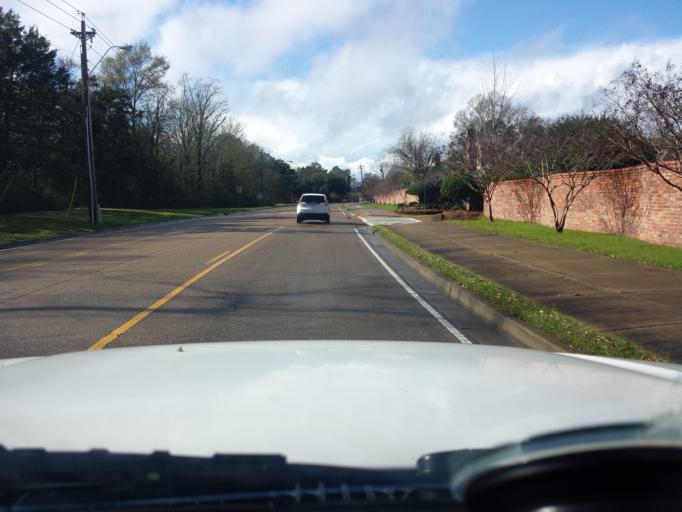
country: US
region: Mississippi
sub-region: Madison County
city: Madison
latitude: 32.4576
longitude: -90.1086
